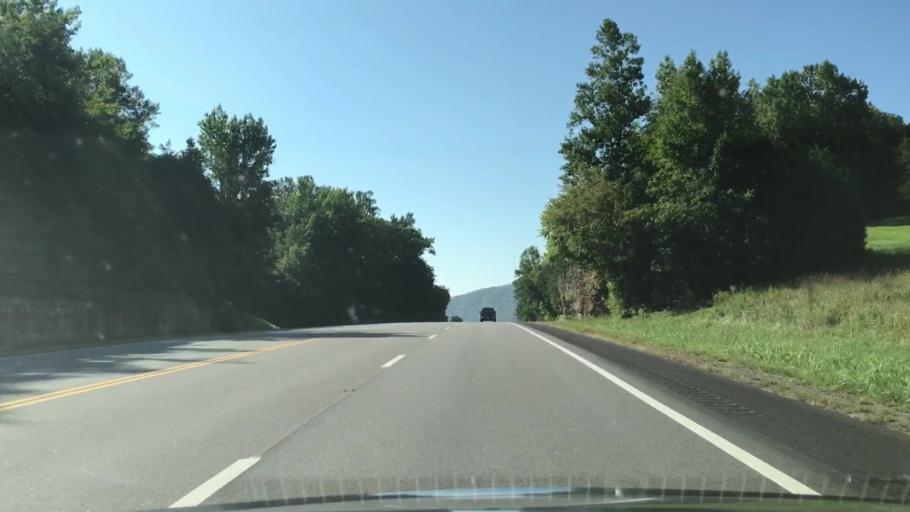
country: US
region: Tennessee
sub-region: Clay County
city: Celina
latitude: 36.5463
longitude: -85.4958
